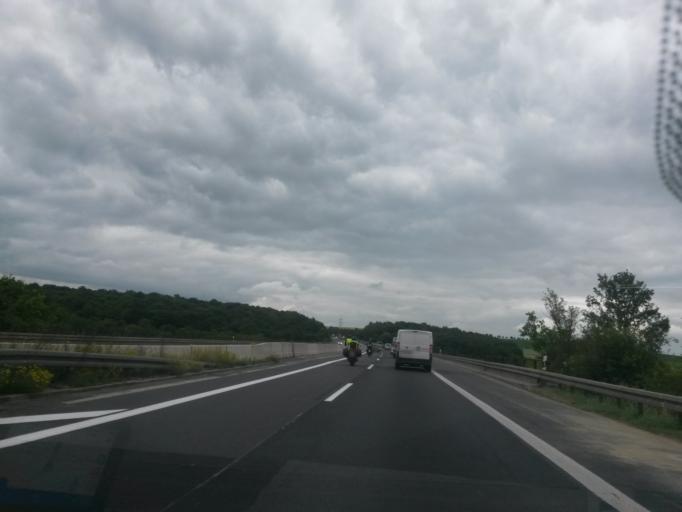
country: DE
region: Bavaria
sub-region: Regierungsbezirk Unterfranken
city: Rottendorf
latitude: 49.8053
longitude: 10.0457
